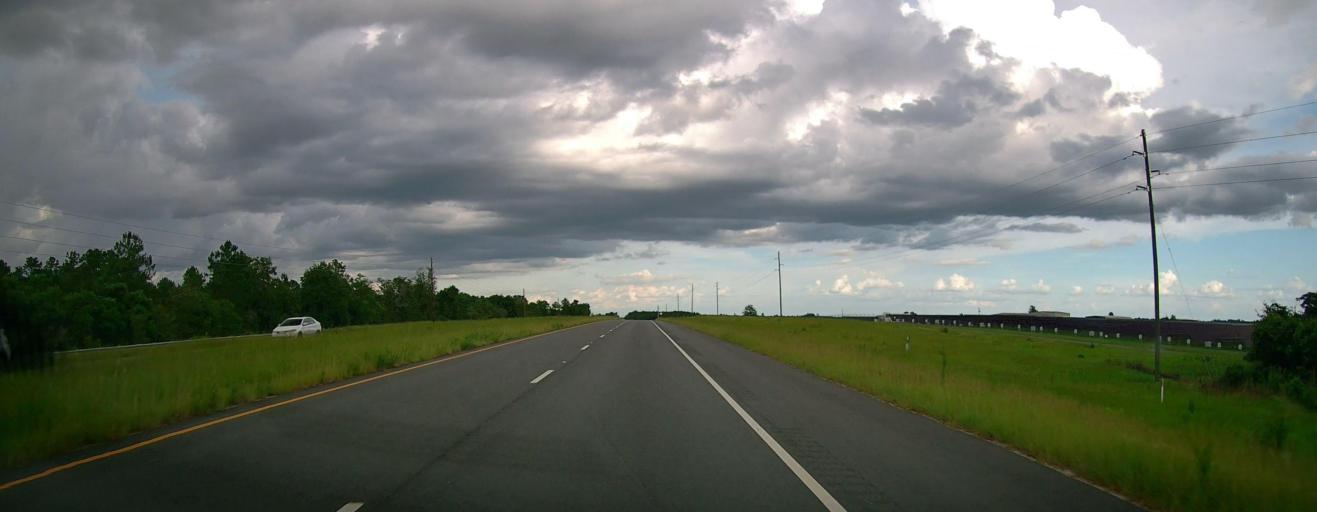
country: US
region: Georgia
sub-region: Taylor County
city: Butler
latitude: 32.5701
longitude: -84.2838
